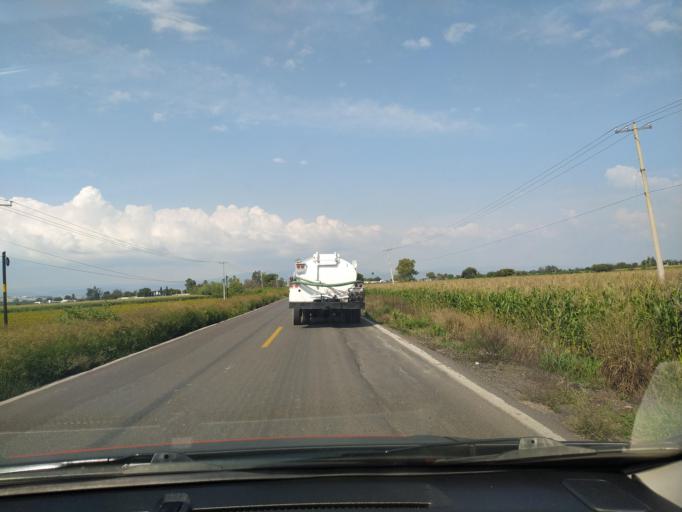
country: MX
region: Guanajuato
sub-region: Leon
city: Malagana (San Antonio del Monte)
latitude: 21.0571
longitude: -101.7418
